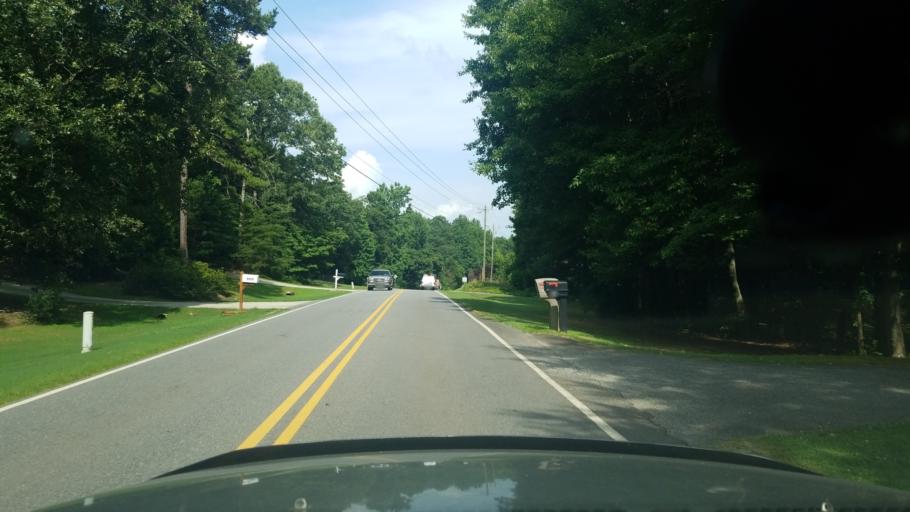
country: US
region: Georgia
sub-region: Dawson County
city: Dawsonville
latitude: 34.3133
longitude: -84.0777
